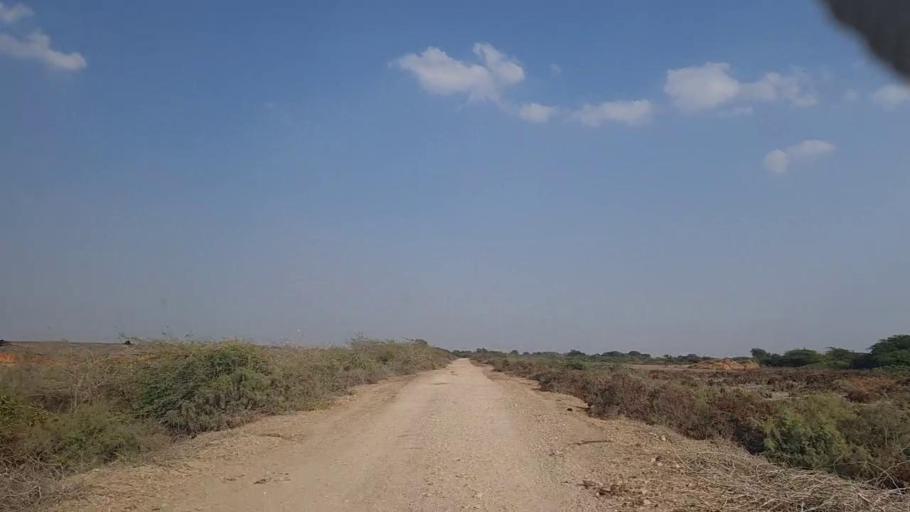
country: PK
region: Sindh
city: Jati
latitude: 24.4299
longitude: 68.3726
